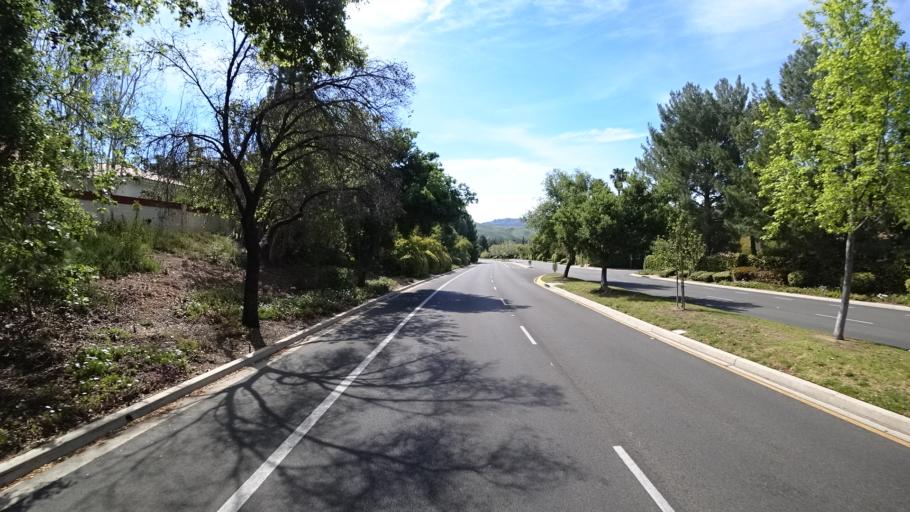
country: US
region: California
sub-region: Ventura County
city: Oak Park
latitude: 34.1893
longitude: -118.7908
